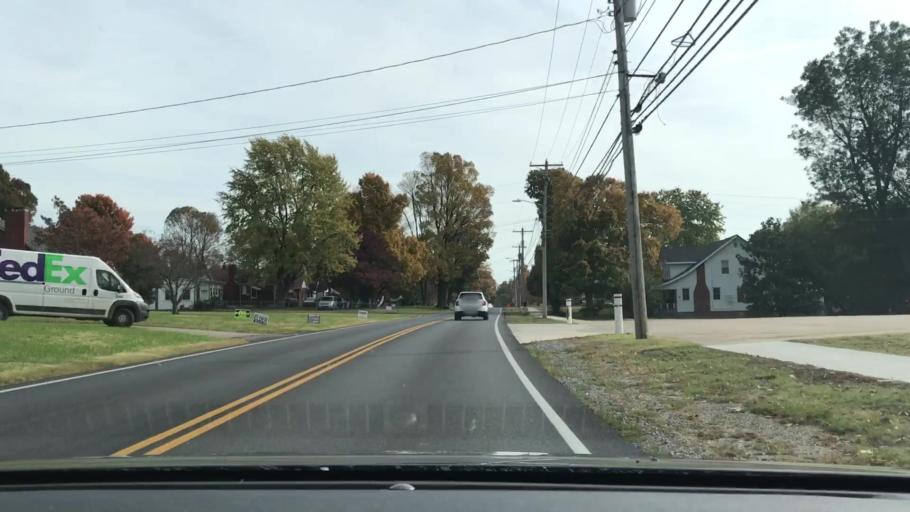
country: US
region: Kentucky
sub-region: Graves County
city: Mayfield
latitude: 36.7420
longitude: -88.6590
